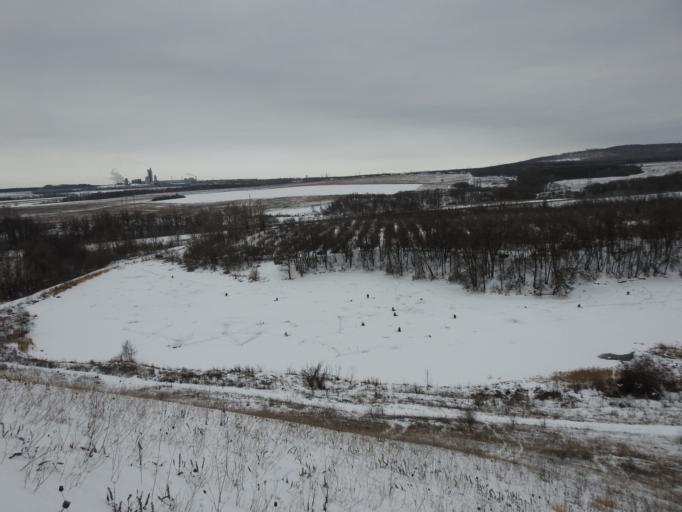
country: RU
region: Saratov
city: Tersa
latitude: 52.1065
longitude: 47.4802
